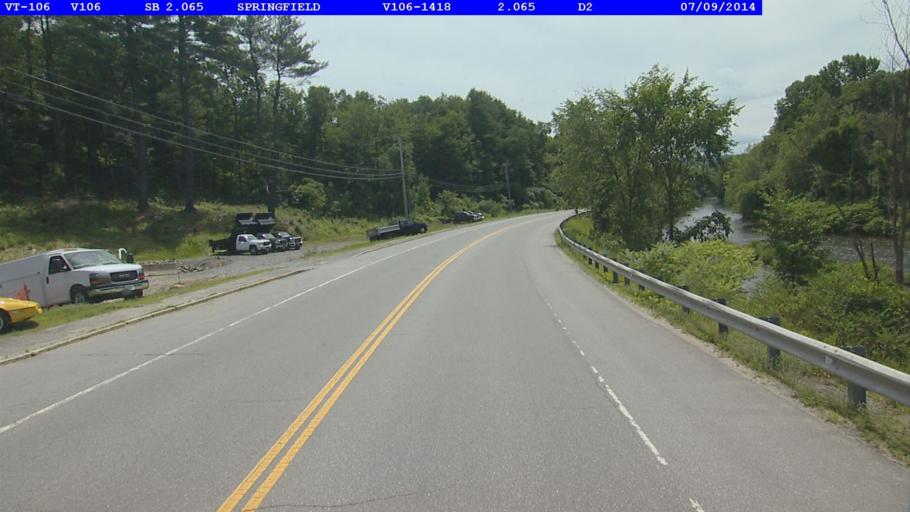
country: US
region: Vermont
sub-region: Windsor County
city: Springfield
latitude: 43.3293
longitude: -72.5126
